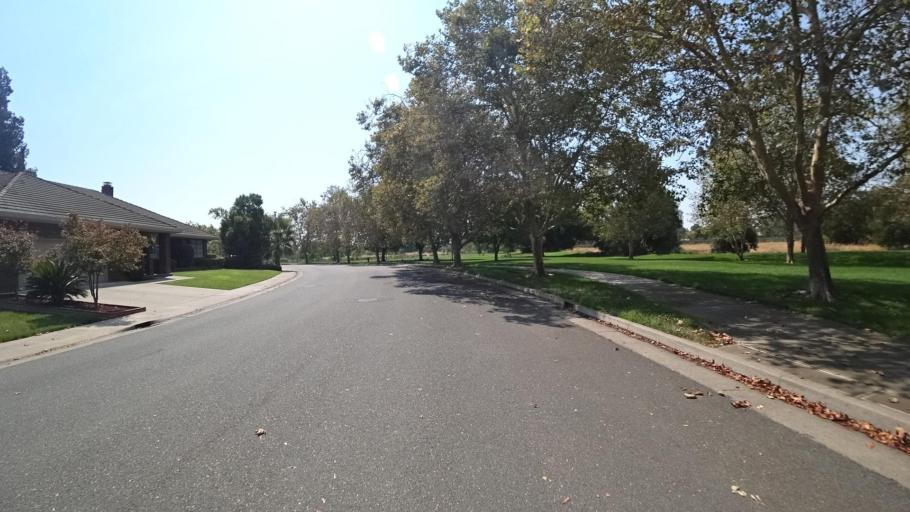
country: US
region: California
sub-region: Sacramento County
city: Elk Grove
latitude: 38.4271
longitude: -121.3806
